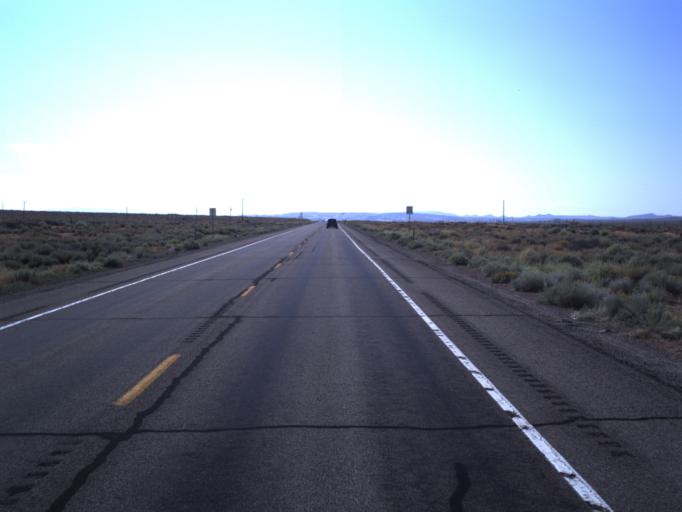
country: US
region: Utah
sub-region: San Juan County
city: Blanding
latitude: 37.1589
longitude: -109.5720
